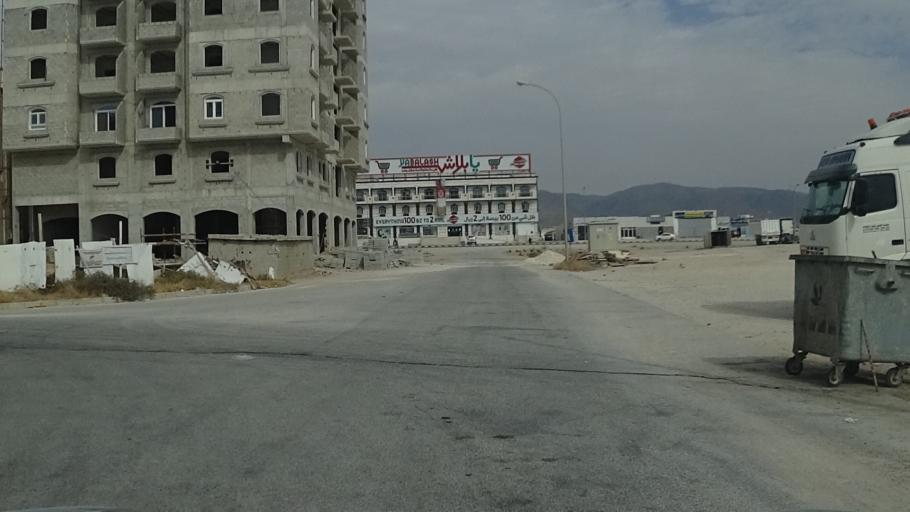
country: OM
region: Zufar
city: Salalah
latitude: 17.0290
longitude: 54.0537
